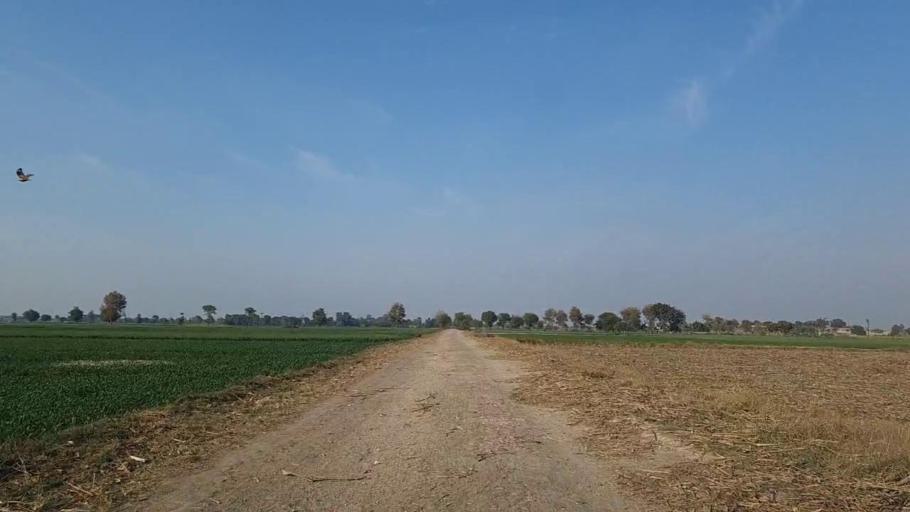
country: PK
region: Sindh
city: Nawabshah
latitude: 26.3744
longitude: 68.4849
